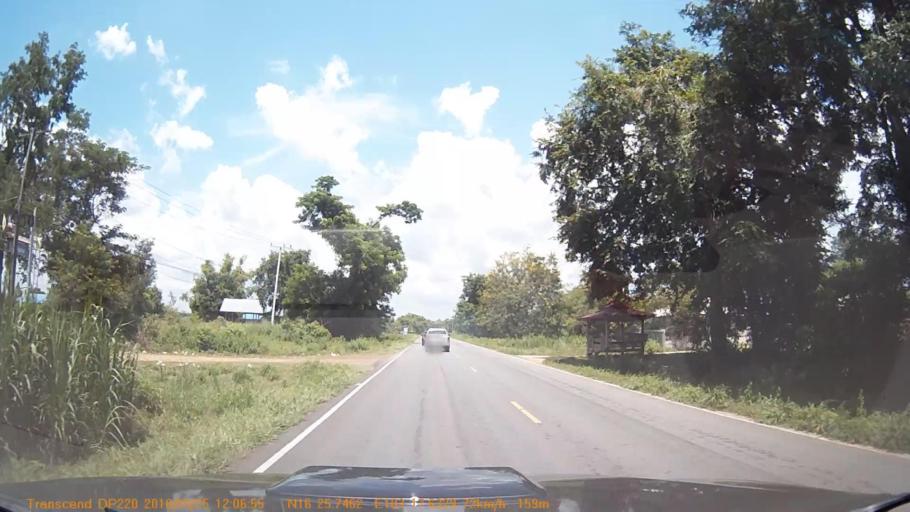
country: TH
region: Kalasin
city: Yang Talat
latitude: 16.4294
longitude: 103.2939
